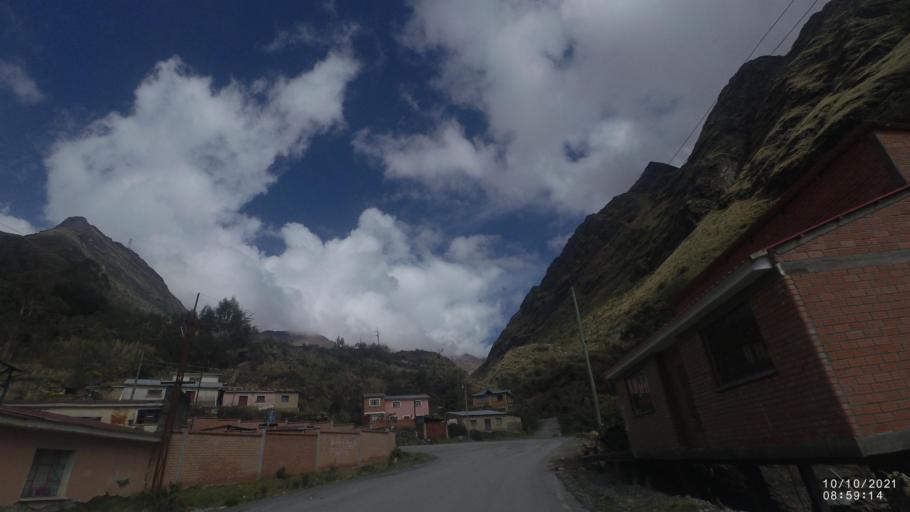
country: BO
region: La Paz
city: Quime
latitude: -16.9962
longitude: -67.2596
